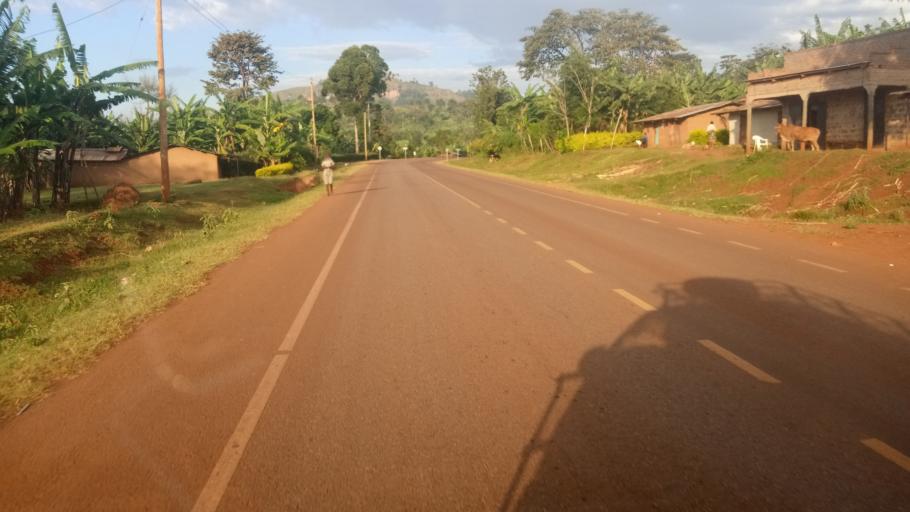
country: UG
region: Eastern Region
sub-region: Kapchorwa District
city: Kapchorwa
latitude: 1.3219
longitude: 34.3445
